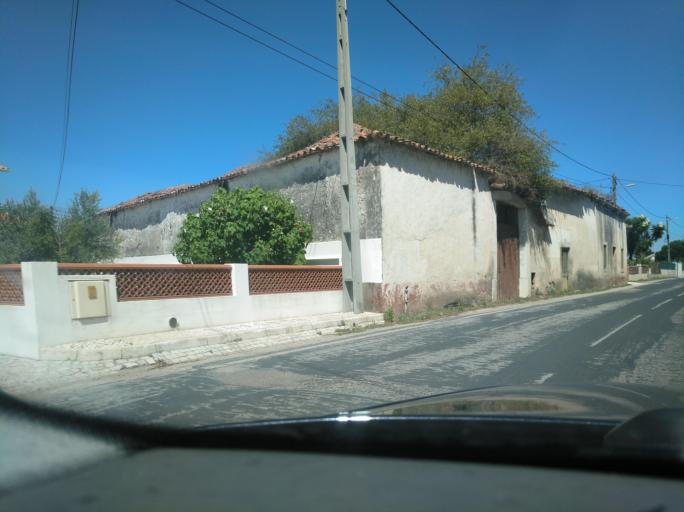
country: PT
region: Leiria
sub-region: Alcobaca
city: Aljubarrota
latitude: 39.5820
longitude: -8.9020
